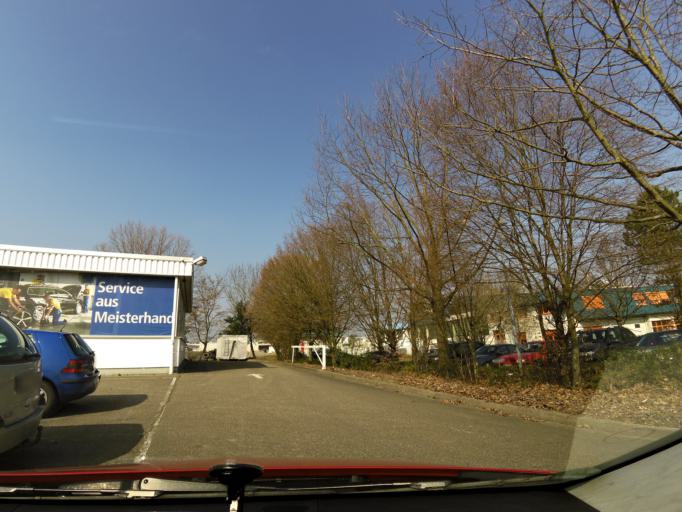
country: DE
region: Baden-Wuerttemberg
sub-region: Freiburg Region
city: Achern
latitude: 48.6356
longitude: 8.0613
